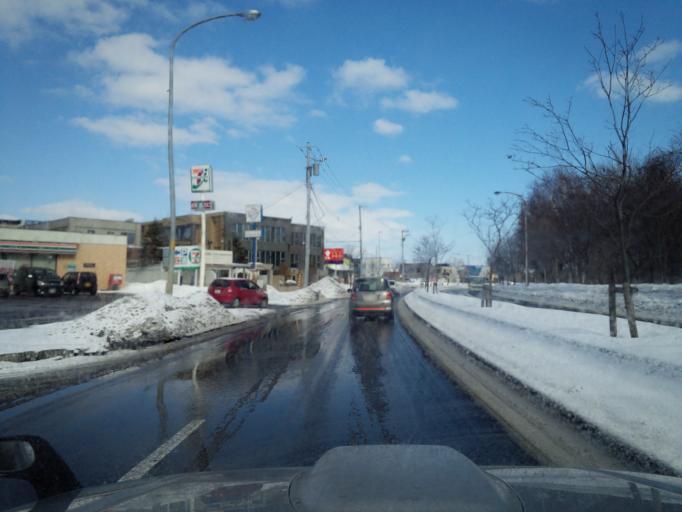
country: JP
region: Hokkaido
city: Kitahiroshima
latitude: 43.0020
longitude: 141.4599
